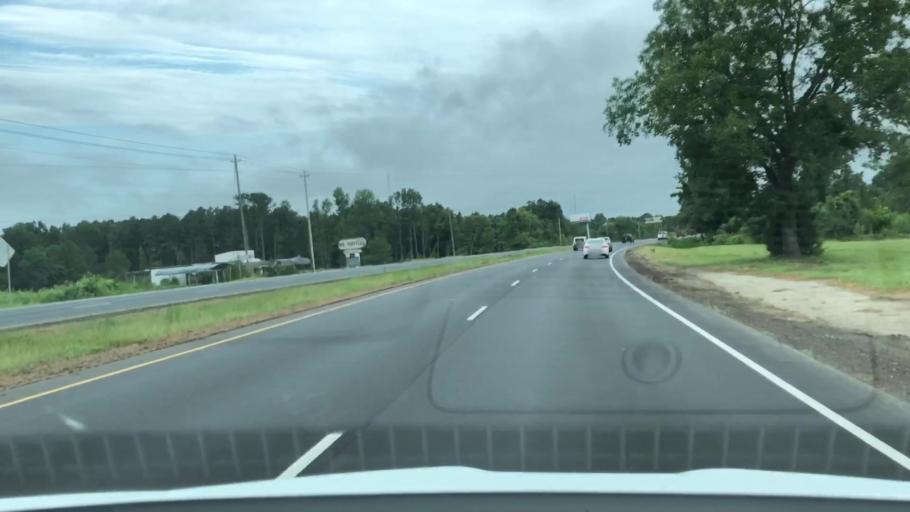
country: US
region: North Carolina
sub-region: Lenoir County
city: Kinston
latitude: 35.2467
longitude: -77.5914
